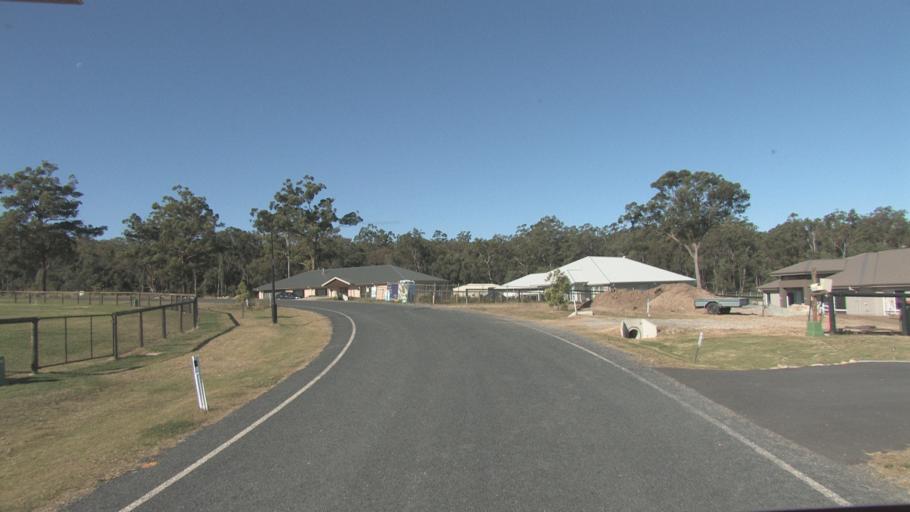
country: AU
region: Queensland
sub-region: Logan
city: Logan Reserve
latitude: -27.7490
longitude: 153.1400
